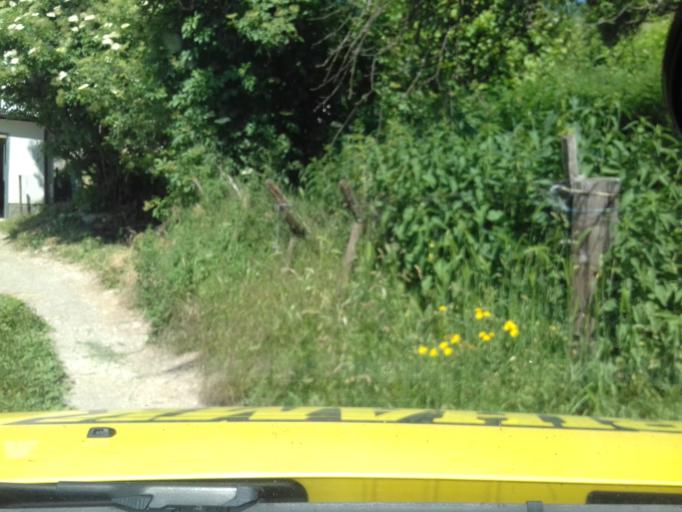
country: BA
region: Federation of Bosnia and Herzegovina
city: Hadzici
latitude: 43.8330
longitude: 18.2087
